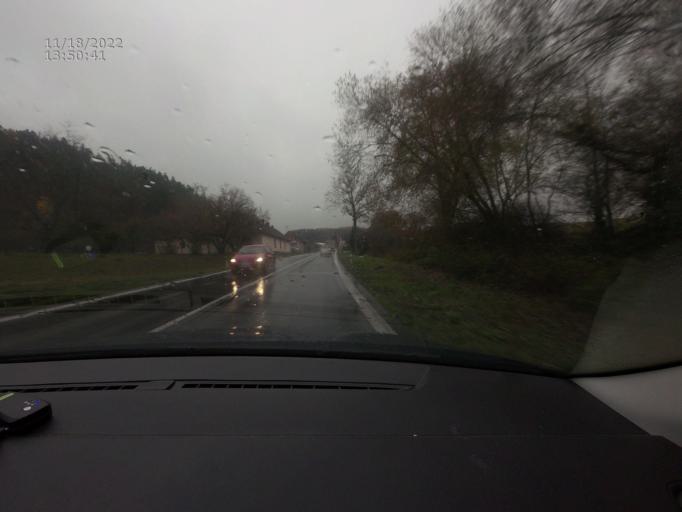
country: CZ
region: Jihocesky
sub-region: Okres Strakonice
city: Blatna
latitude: 49.4033
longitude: 13.9067
